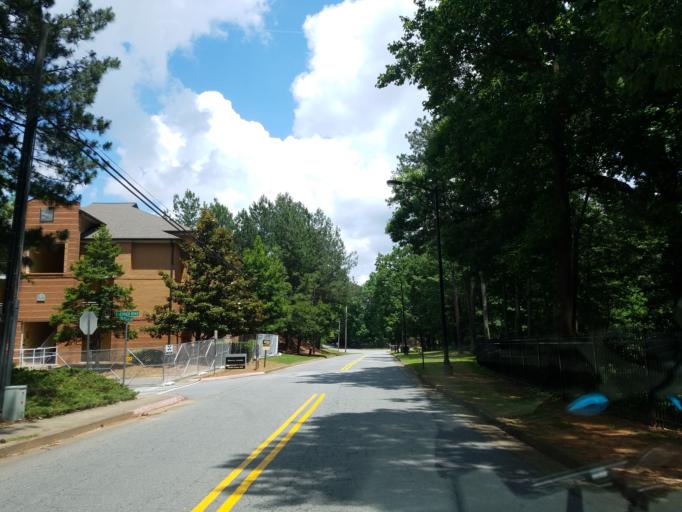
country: US
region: Georgia
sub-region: Cobb County
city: Fair Oaks
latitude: 33.9364
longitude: -84.5178
